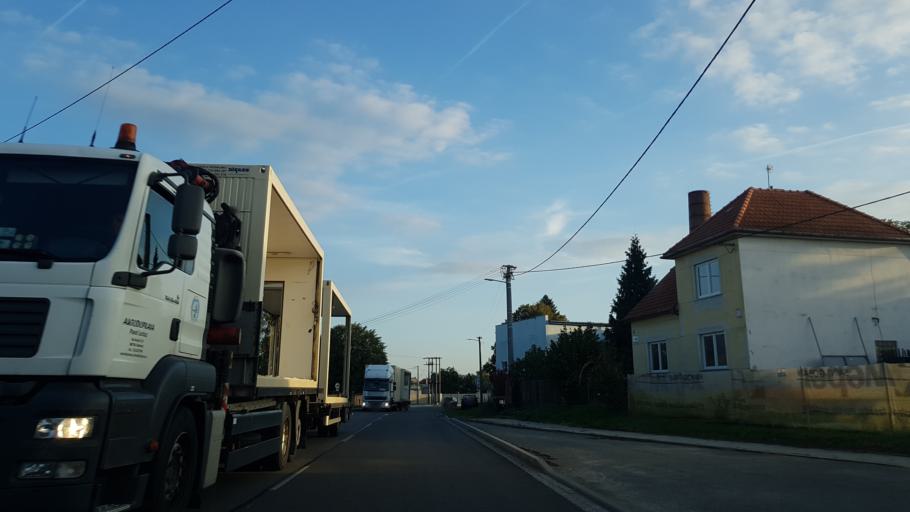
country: CZ
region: Zlin
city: Nedakonice
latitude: 49.0346
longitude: 17.3815
